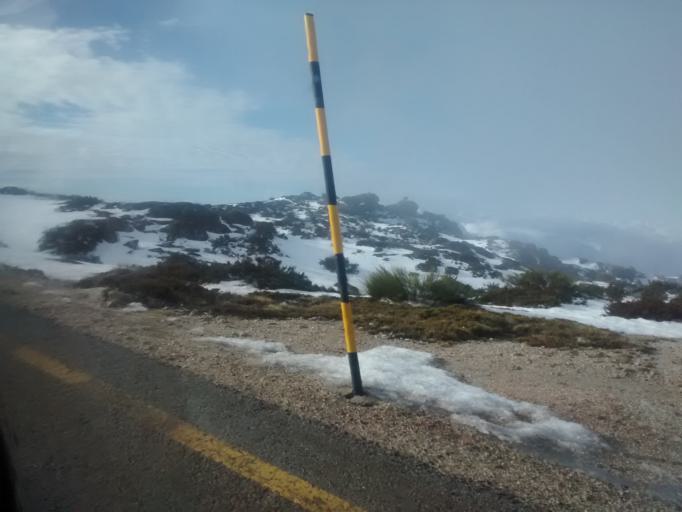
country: PT
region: Guarda
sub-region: Seia
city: Seia
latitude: 40.3471
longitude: -7.6630
